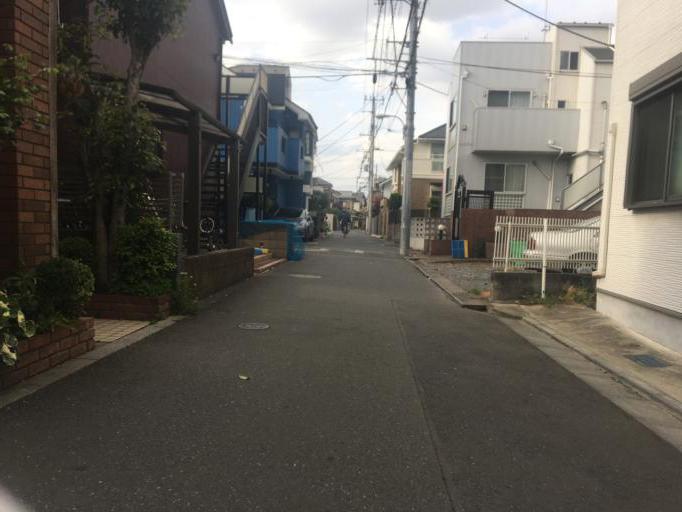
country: JP
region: Tokyo
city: Tokyo
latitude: 35.6988
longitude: 139.6283
